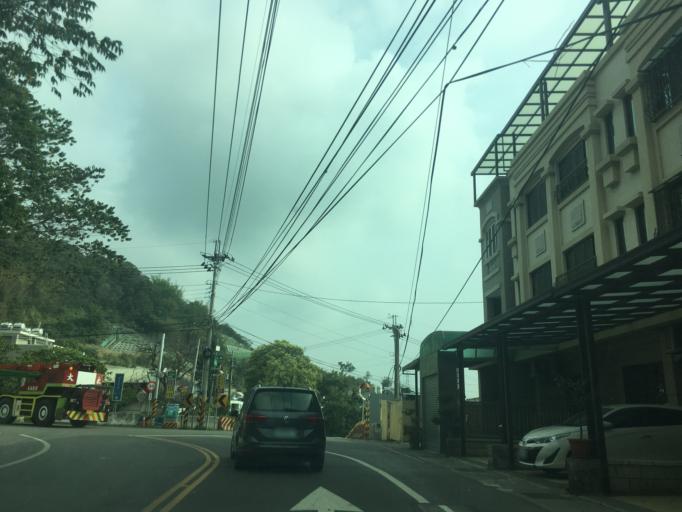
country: TW
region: Taiwan
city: Fengyuan
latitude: 24.2374
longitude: 120.7344
